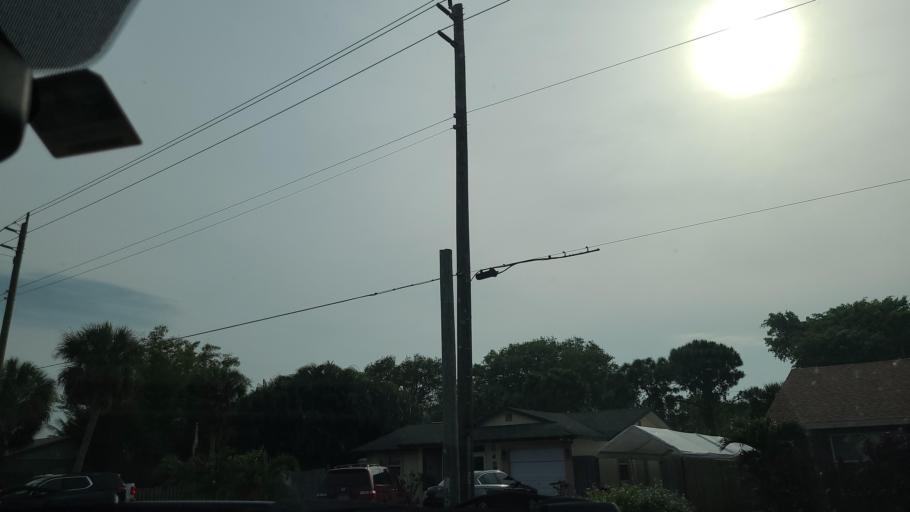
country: US
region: Florida
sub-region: Indian River County
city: Sebastian
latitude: 27.8080
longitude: -80.4864
